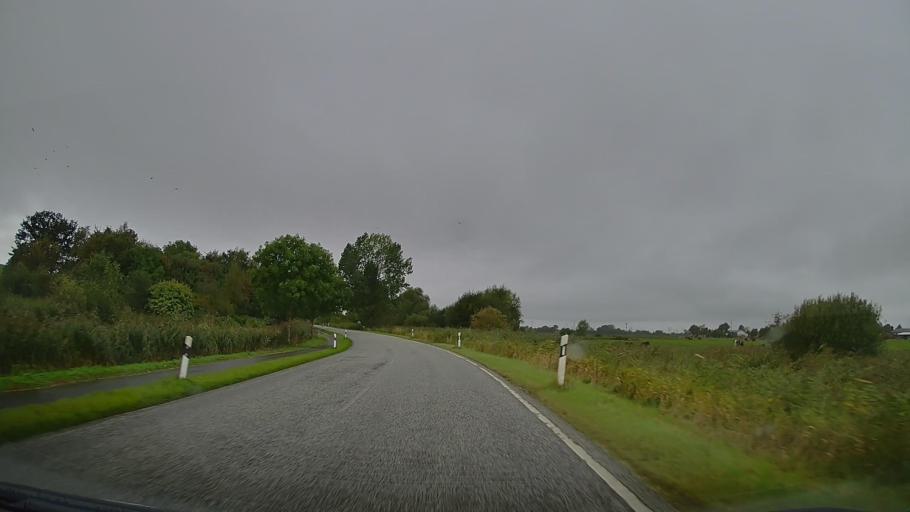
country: DE
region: Schleswig-Holstein
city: Sankt Margarethen
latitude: 53.8788
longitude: 9.2744
